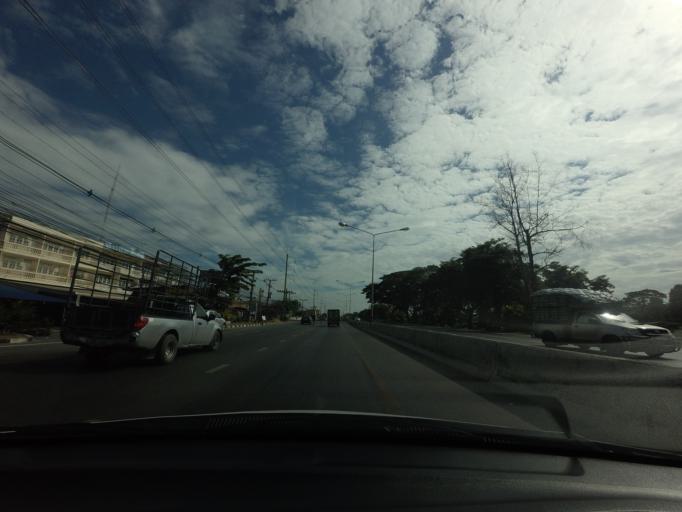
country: TH
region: Pathum Thani
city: Ban Rangsit
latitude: 14.0524
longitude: 100.8232
